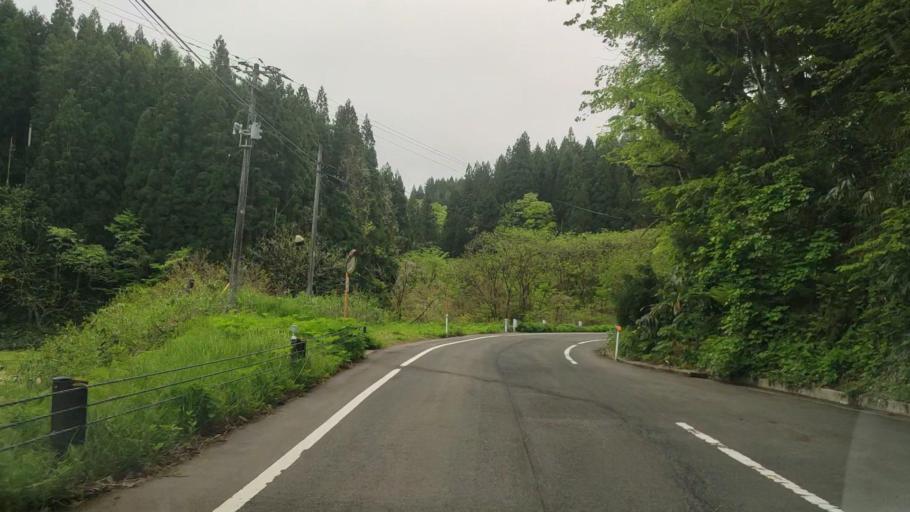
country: JP
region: Niigata
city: Gosen
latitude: 37.7145
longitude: 139.1234
